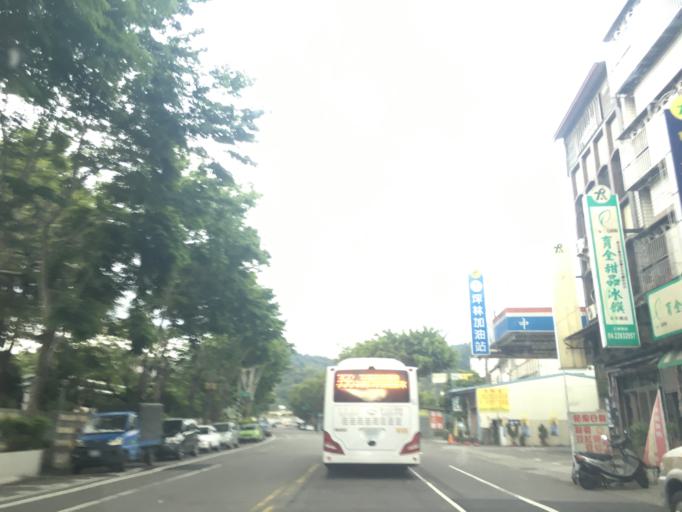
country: TW
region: Taiwan
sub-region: Taichung City
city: Taichung
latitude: 24.1503
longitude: 120.7307
